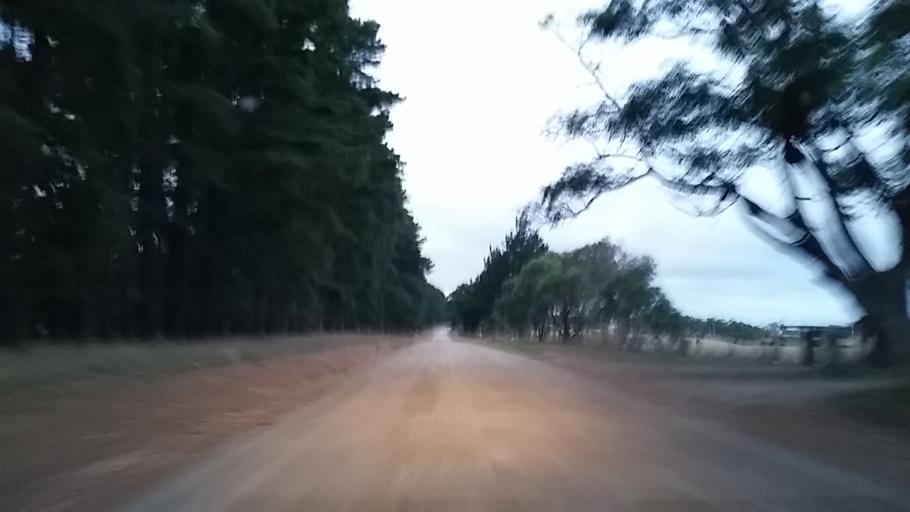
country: AU
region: South Australia
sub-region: Yankalilla
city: Normanville
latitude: -35.6099
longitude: 138.1853
